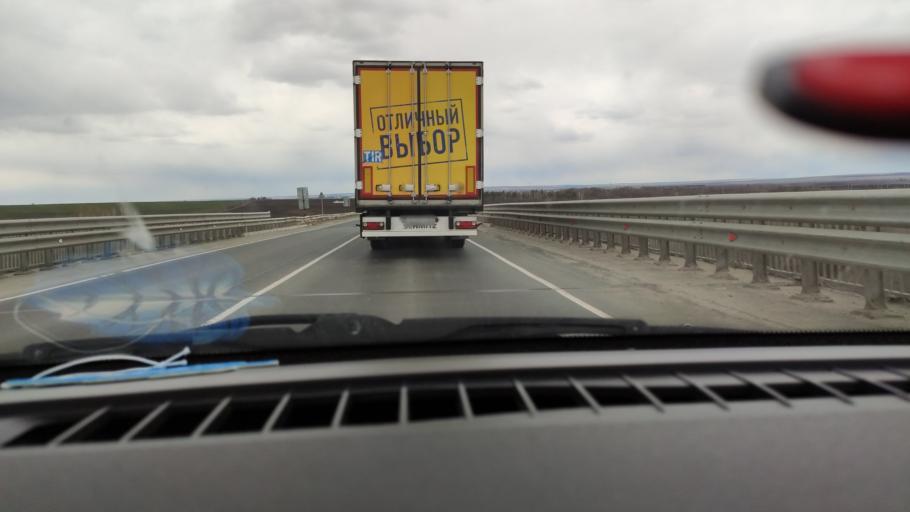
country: RU
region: Saratov
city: Sennoy
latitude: 52.1592
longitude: 47.0372
